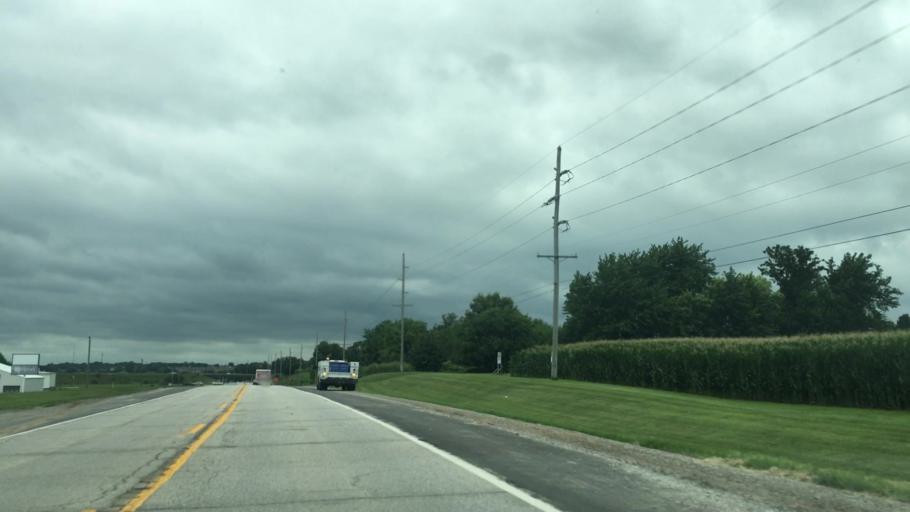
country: US
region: Iowa
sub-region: Johnson County
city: Tiffin
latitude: 41.7026
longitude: -91.6332
